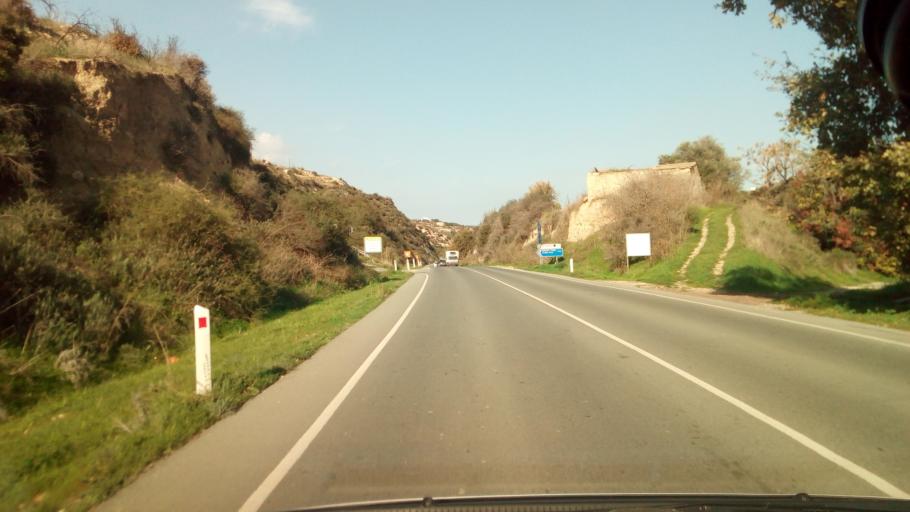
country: CY
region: Pafos
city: Polis
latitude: 34.9698
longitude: 32.4533
